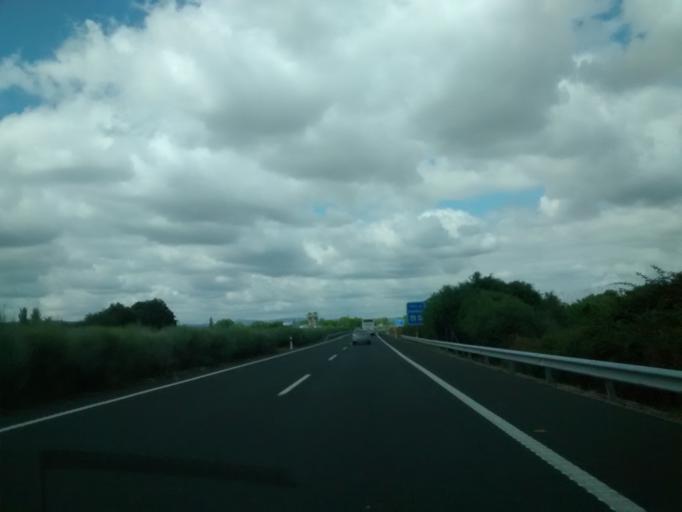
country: ES
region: Extremadura
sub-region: Provincia de Caceres
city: Millanes
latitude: 39.8576
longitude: -5.6156
